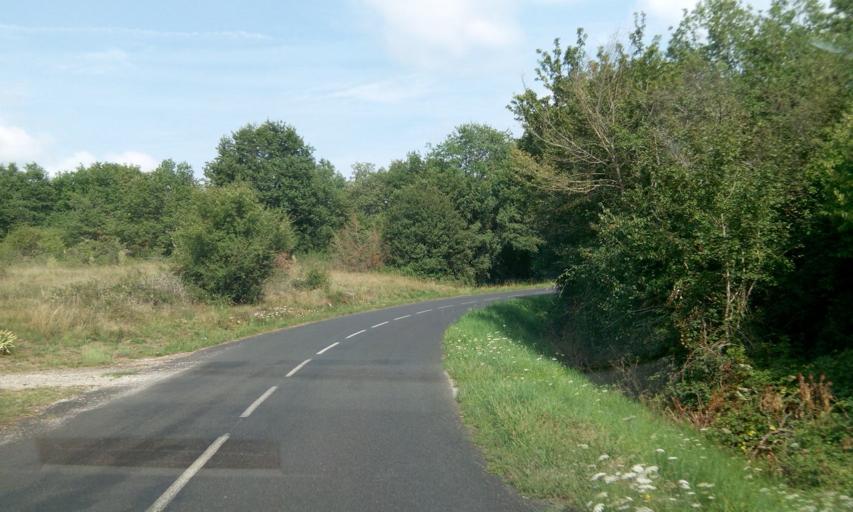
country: FR
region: Limousin
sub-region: Departement de la Correze
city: Brive-la-Gaillarde
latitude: 45.0534
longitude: 1.5288
